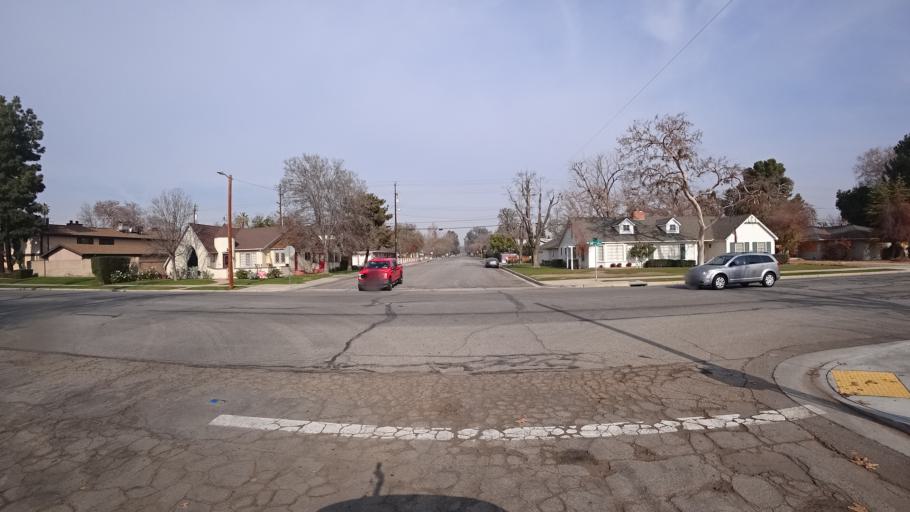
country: US
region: California
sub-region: Kern County
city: Bakersfield
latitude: 35.3752
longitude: -119.0363
